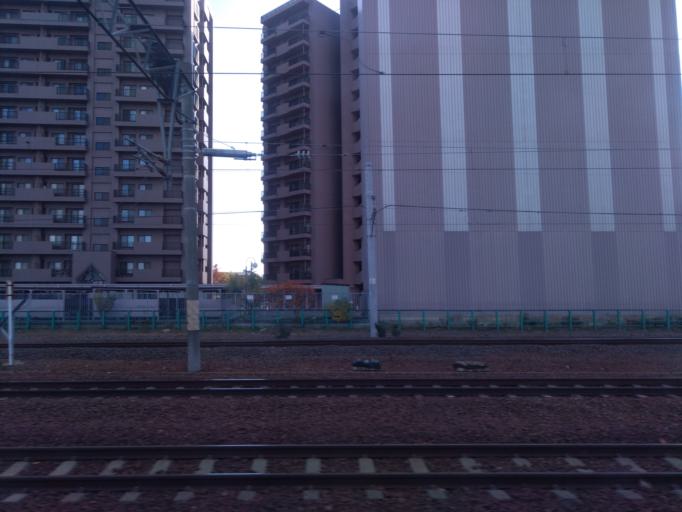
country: JP
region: Hokkaido
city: Sapporo
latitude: 43.0687
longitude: 141.3751
